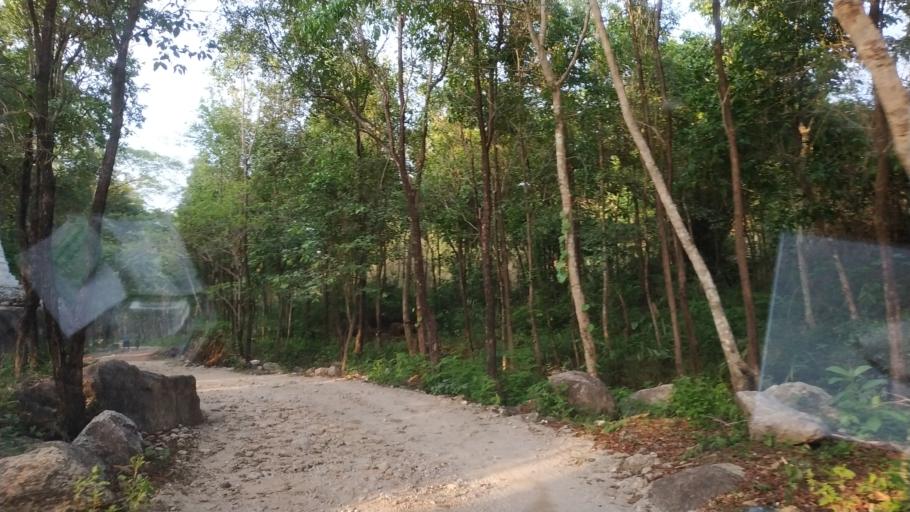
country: MM
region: Mon
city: Kyaikto
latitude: 17.4380
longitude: 97.0398
